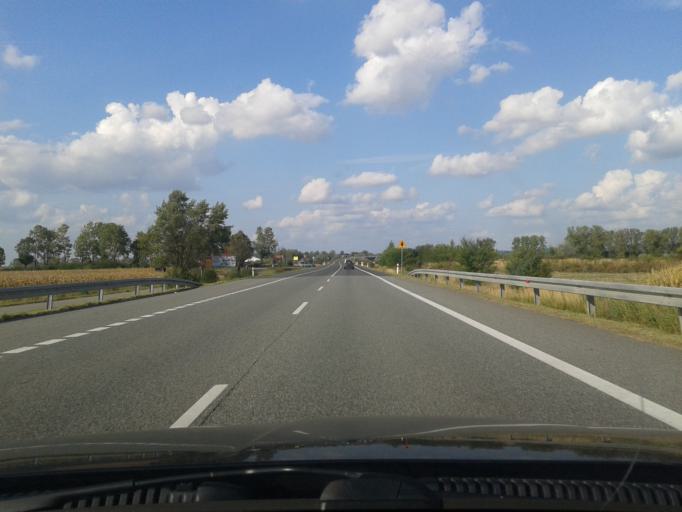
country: PL
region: Silesian Voivodeship
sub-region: Powiat wodzislawski
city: Olza
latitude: 49.9466
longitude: 18.3270
